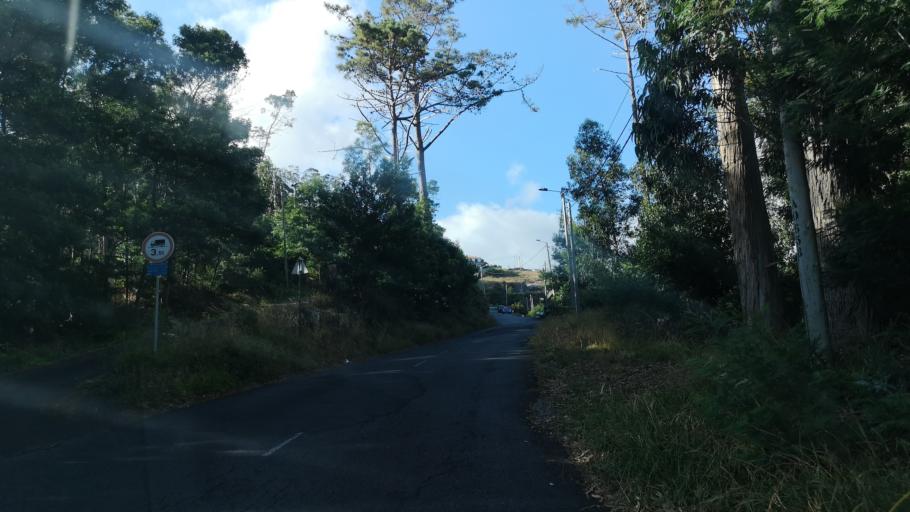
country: PT
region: Madeira
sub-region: Santa Cruz
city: Camacha
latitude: 32.6638
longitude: -16.8372
